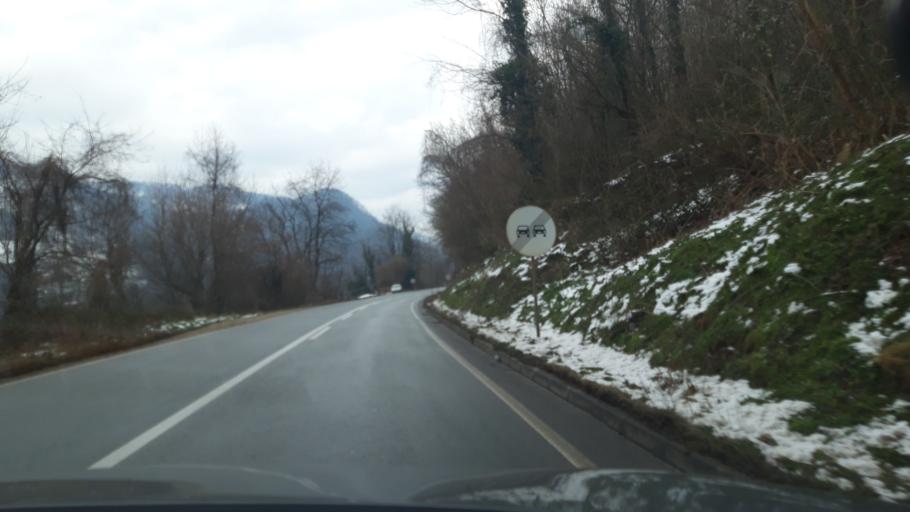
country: RS
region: Central Serbia
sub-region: Macvanski Okrug
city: Mali Zvornik
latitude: 44.3380
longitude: 19.1315
